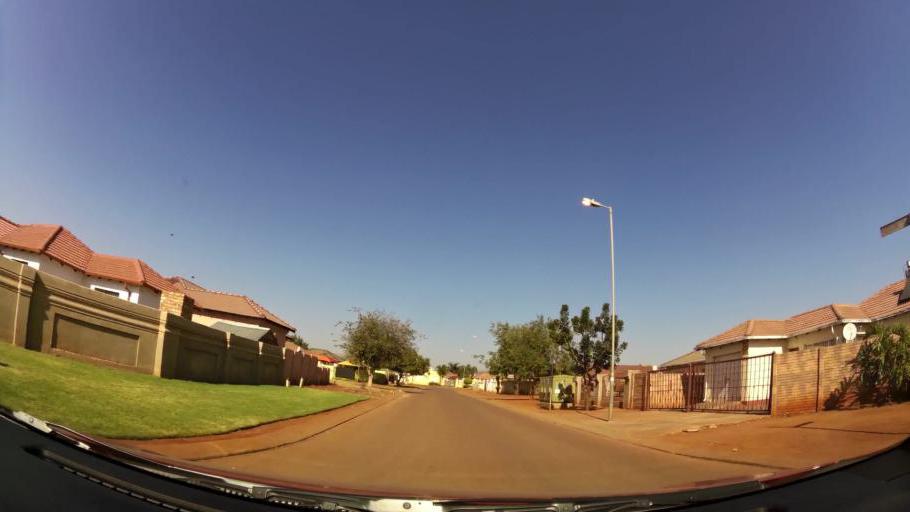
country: ZA
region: North-West
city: Ga-Rankuwa
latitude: -25.6364
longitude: 28.0818
